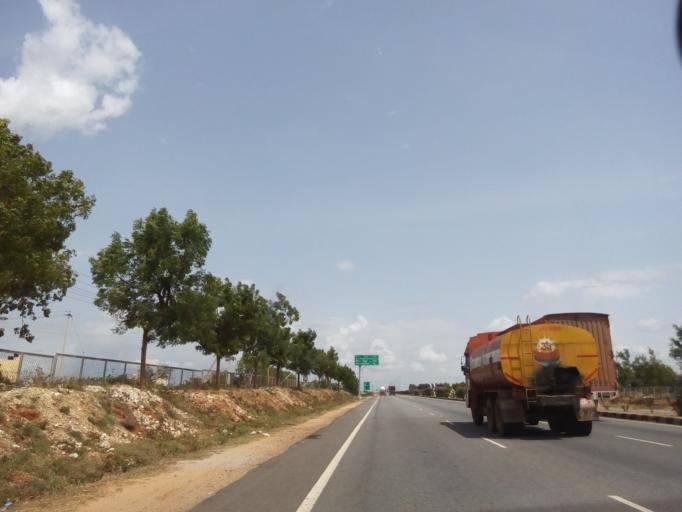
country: IN
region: Karnataka
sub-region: Tumkur
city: Sira
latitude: 13.7428
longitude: 76.8893
